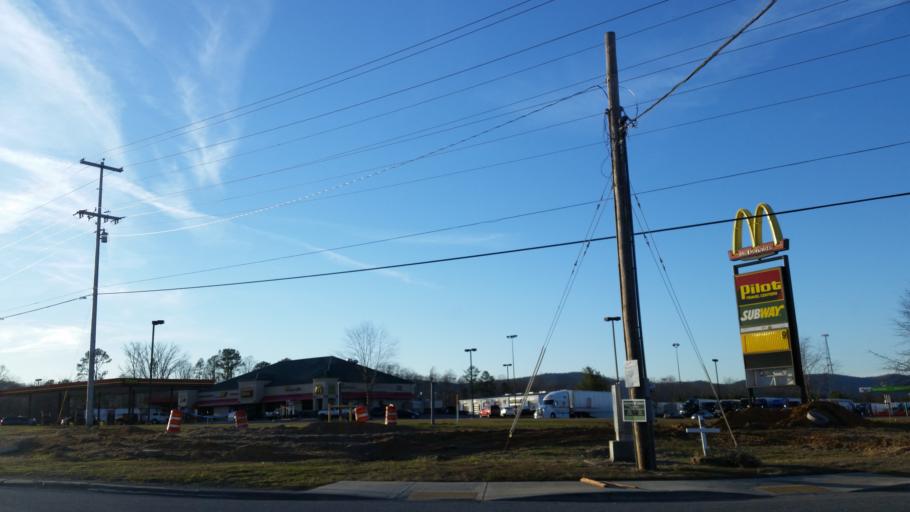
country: US
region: Georgia
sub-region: Whitfield County
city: Dalton
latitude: 34.6553
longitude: -84.9786
